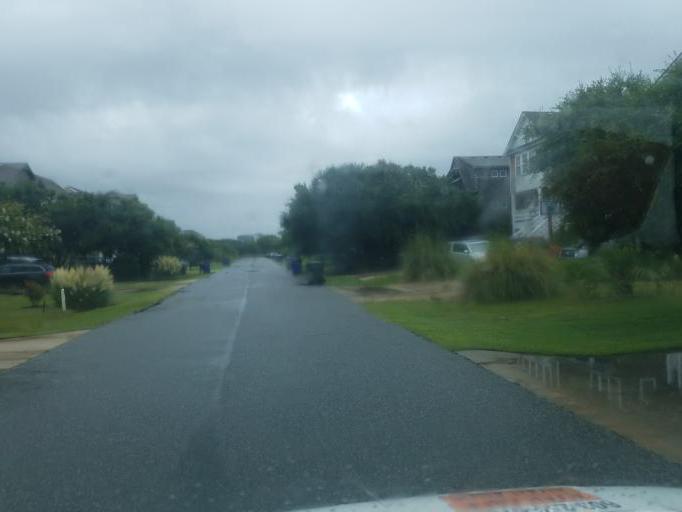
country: US
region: North Carolina
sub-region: Dare County
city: Nags Head
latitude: 35.9714
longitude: -75.6338
